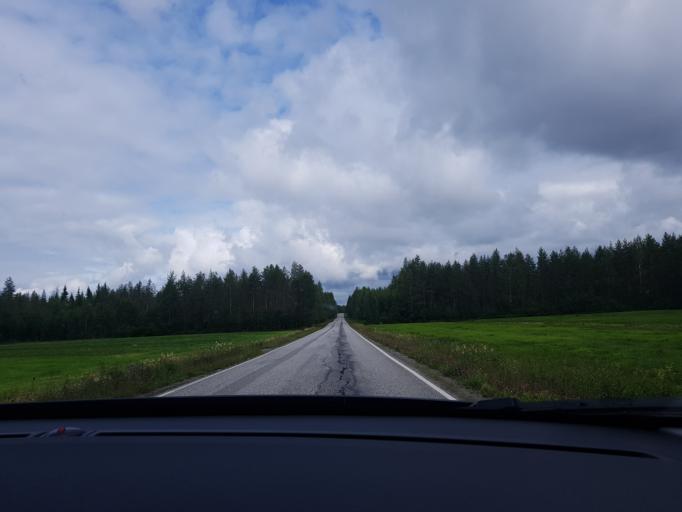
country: FI
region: Kainuu
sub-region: Kehys-Kainuu
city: Kuhmo
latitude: 64.2005
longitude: 29.4517
